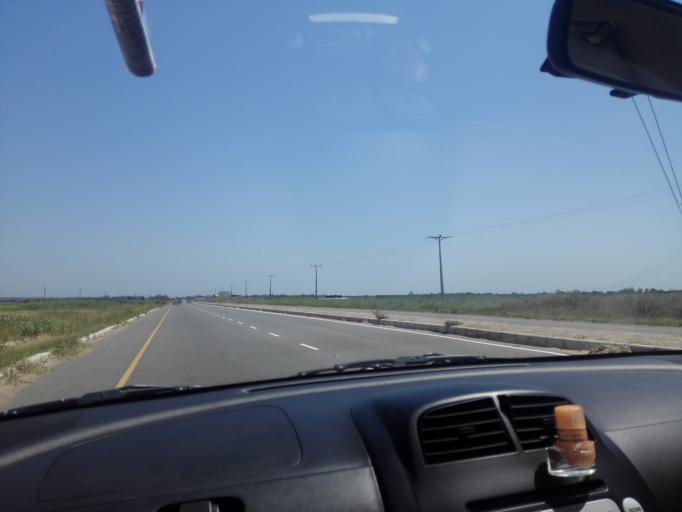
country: MZ
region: Maputo City
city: Maputo
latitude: -25.8332
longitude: 32.6720
